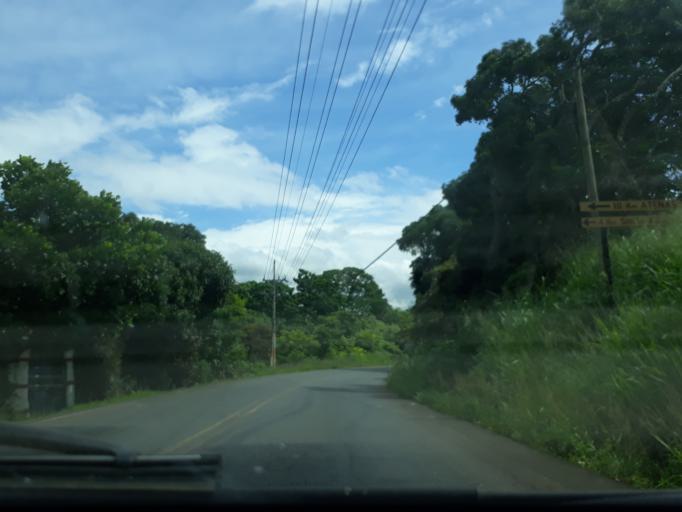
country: CR
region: Alajuela
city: Atenas
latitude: 10.0261
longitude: -84.3565
